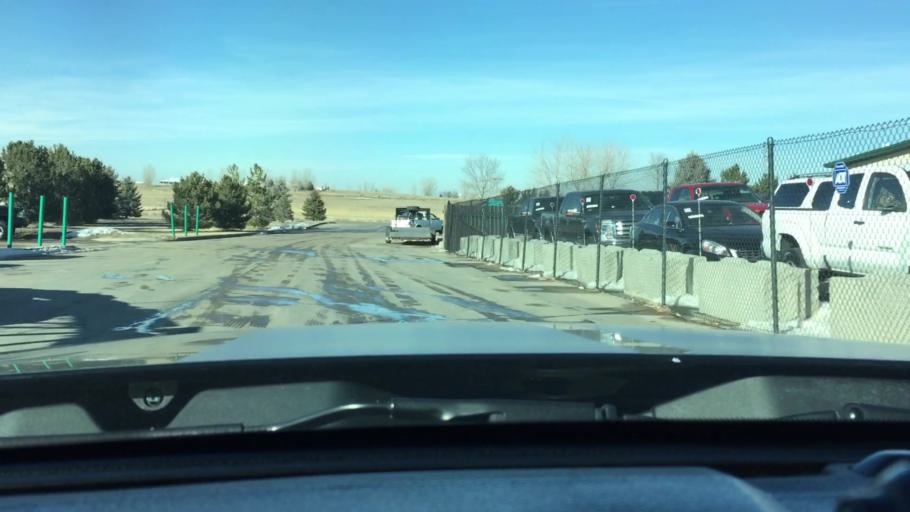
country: US
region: Colorado
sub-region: Weld County
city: Johnstown
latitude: 40.3625
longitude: -104.9771
